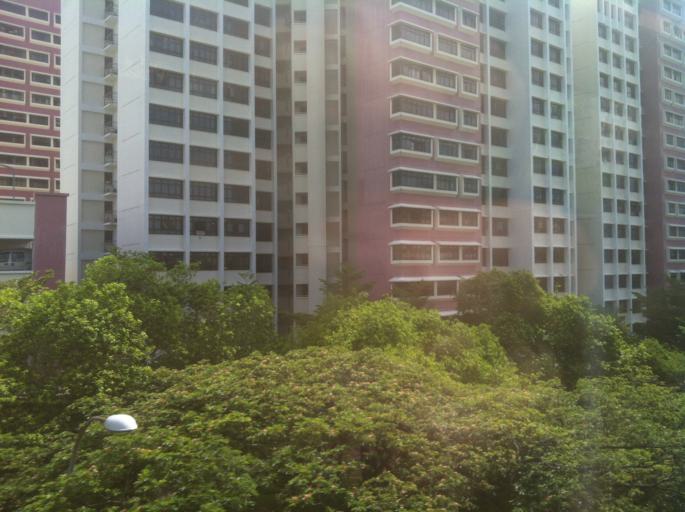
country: SG
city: Singapore
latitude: 1.3245
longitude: 103.9331
